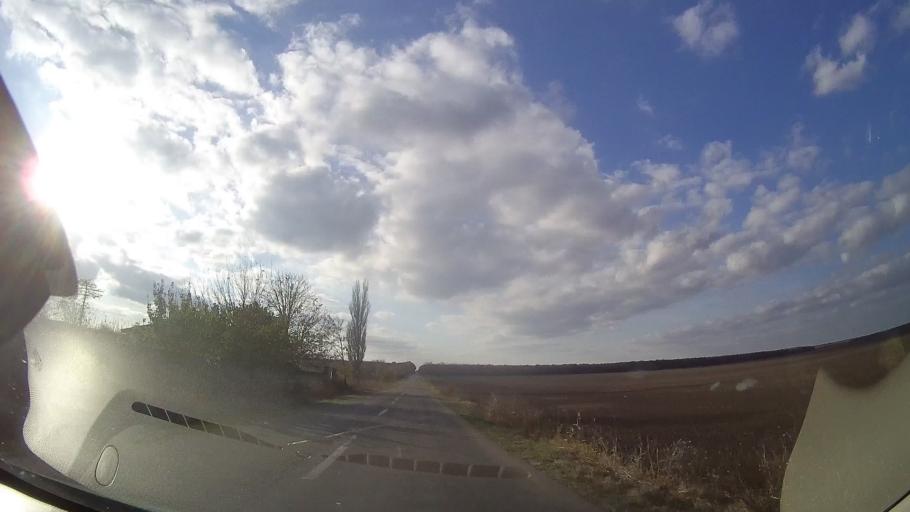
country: RO
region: Constanta
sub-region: Comuna Comana
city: Comana
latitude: 43.8192
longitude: 28.2904
